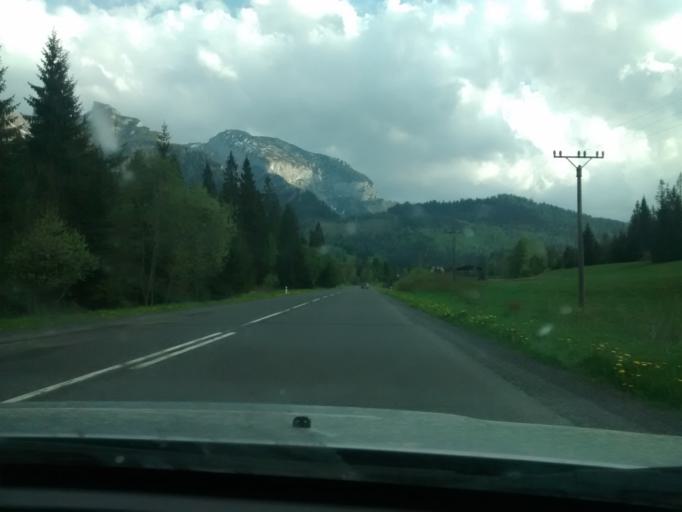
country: PL
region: Lesser Poland Voivodeship
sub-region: Powiat tatrzanski
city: Bukowina Tatrzanska
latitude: 49.2858
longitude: 20.1750
